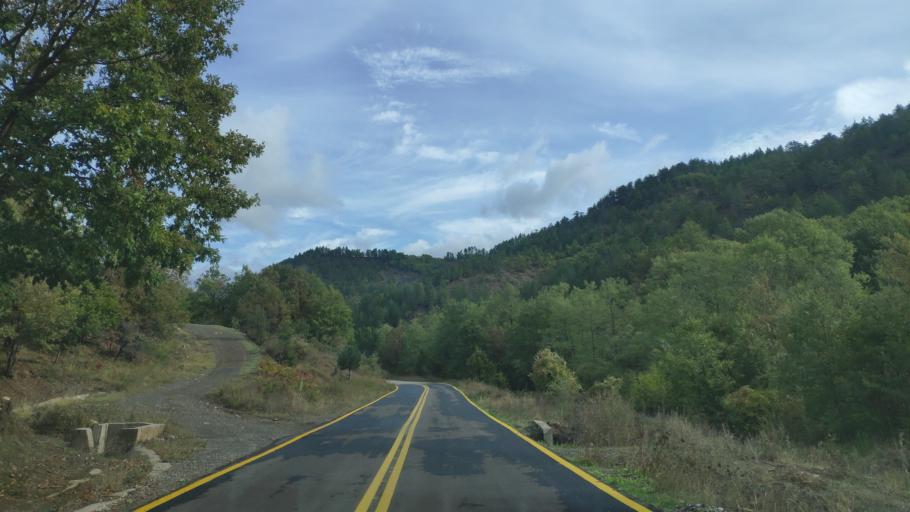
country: GR
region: West Macedonia
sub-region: Nomos Kastorias
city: Nestorio
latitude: 40.2337
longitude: 20.9886
